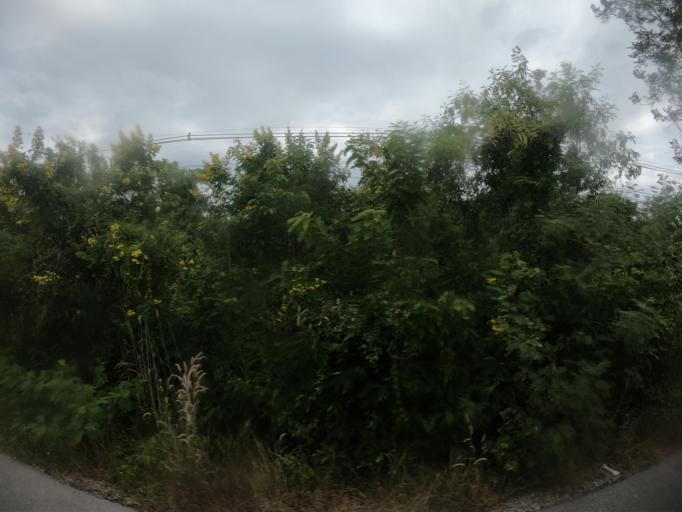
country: TH
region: Maha Sarakham
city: Kantharawichai
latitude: 16.3378
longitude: 103.2196
